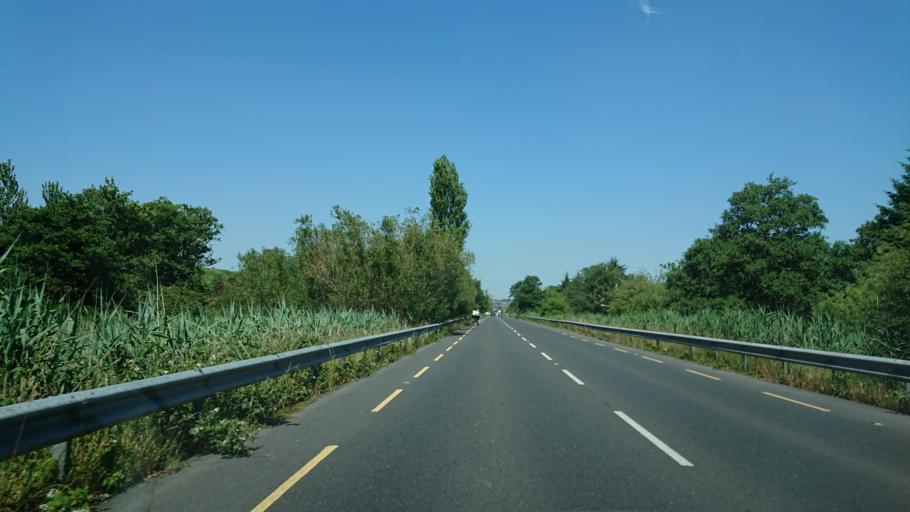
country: IE
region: Munster
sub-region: Waterford
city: Waterford
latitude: 52.2396
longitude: -7.1210
